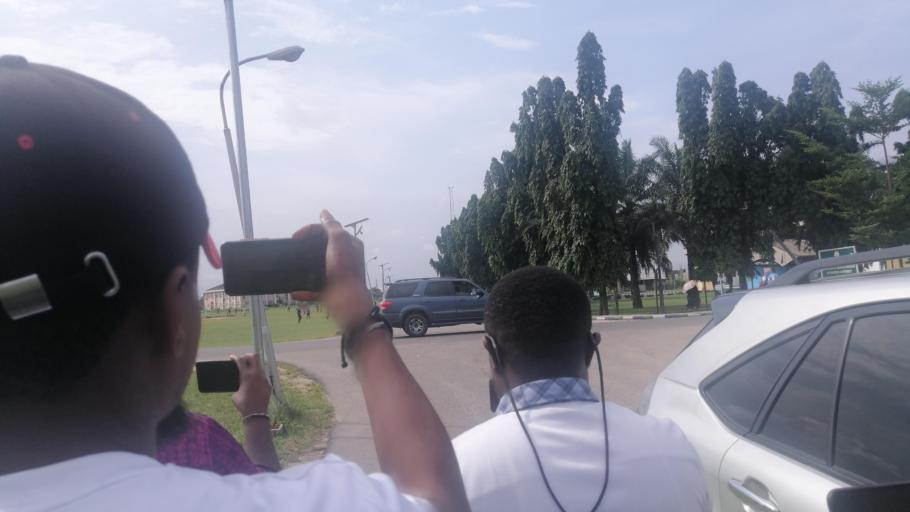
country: NG
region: Rivers
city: Port Harcourt
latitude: 4.8003
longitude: 6.9803
